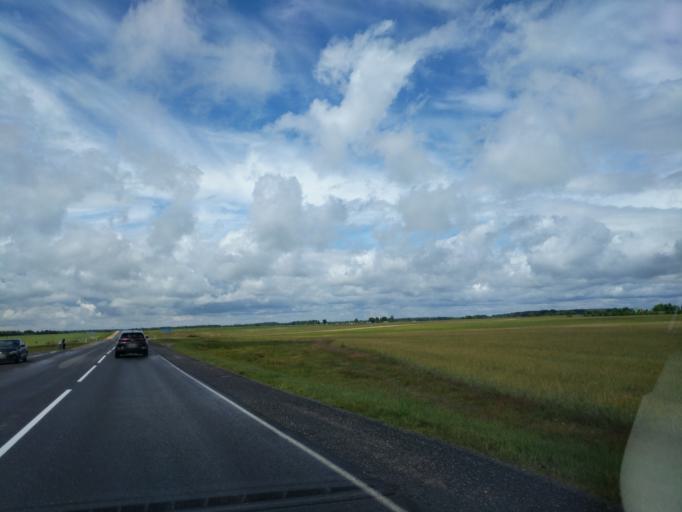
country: BY
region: Minsk
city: Il'ya
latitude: 54.3880
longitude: 27.3560
